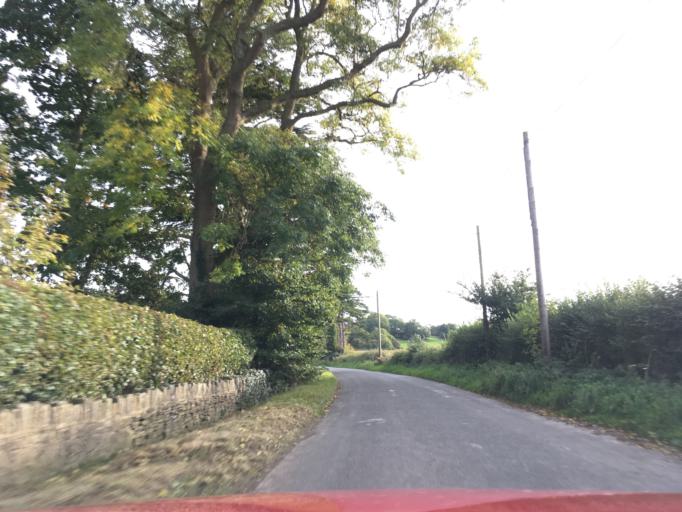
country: GB
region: England
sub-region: South Gloucestershire
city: Alveston
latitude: 51.6063
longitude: -2.5474
